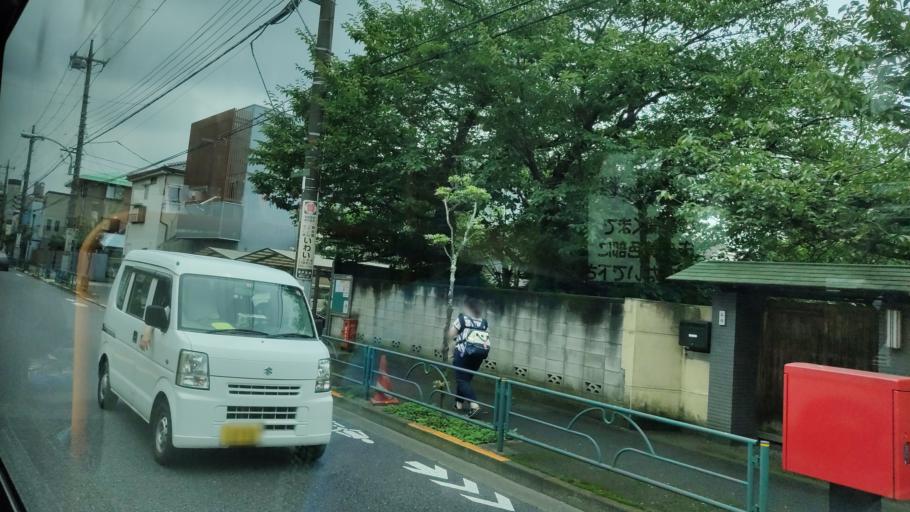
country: JP
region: Chiba
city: Matsudo
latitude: 35.7352
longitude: 139.8608
